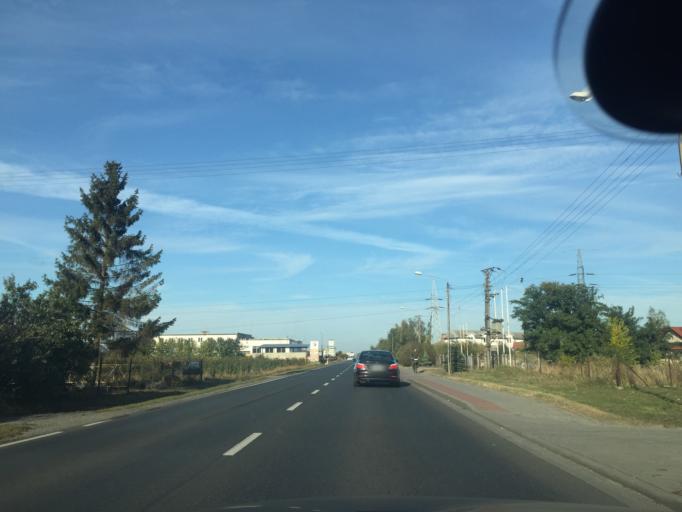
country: PL
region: Kujawsko-Pomorskie
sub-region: Powiat inowroclawski
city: Inowroclaw
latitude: 52.7369
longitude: 18.2445
